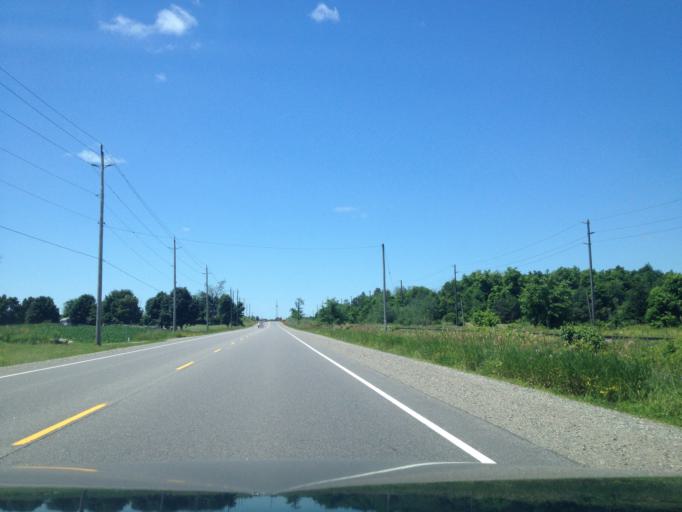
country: CA
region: Ontario
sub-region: Wellington County
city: Guelph
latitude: 43.6302
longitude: -80.0715
